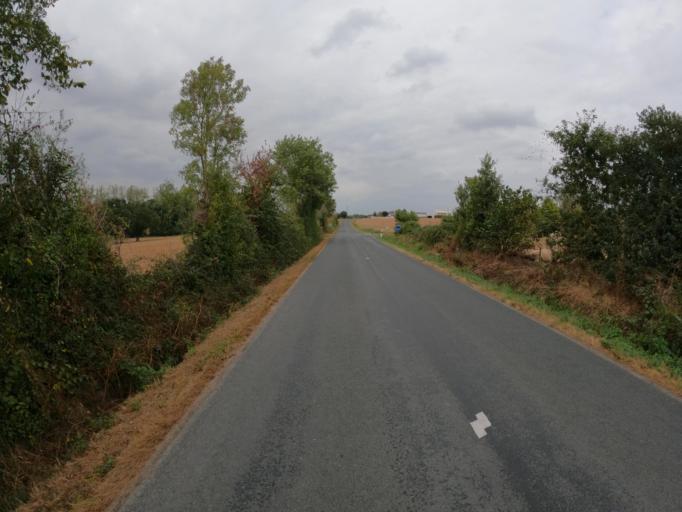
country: FR
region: Pays de la Loire
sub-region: Departement de la Vendee
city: Les Landes-Genusson
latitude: 46.9772
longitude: -1.1123
